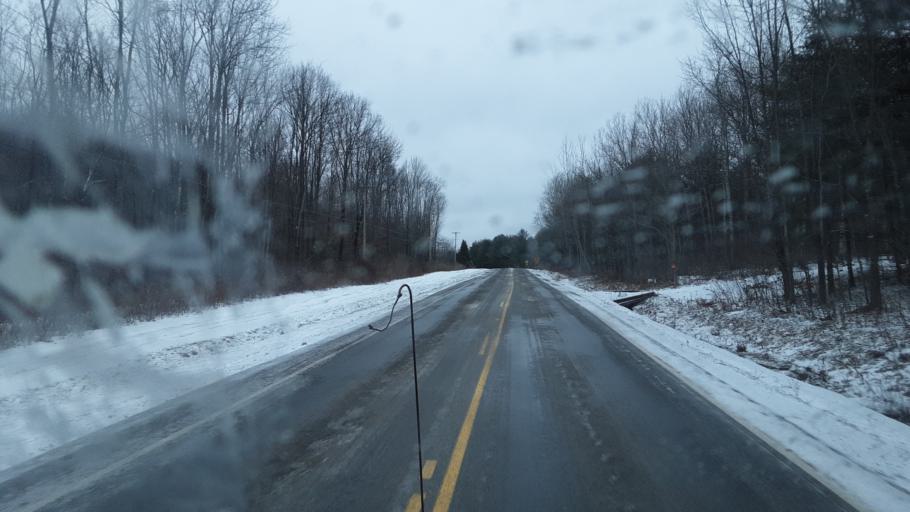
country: US
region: New York
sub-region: Allegany County
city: Friendship
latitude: 42.2250
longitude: -78.1411
